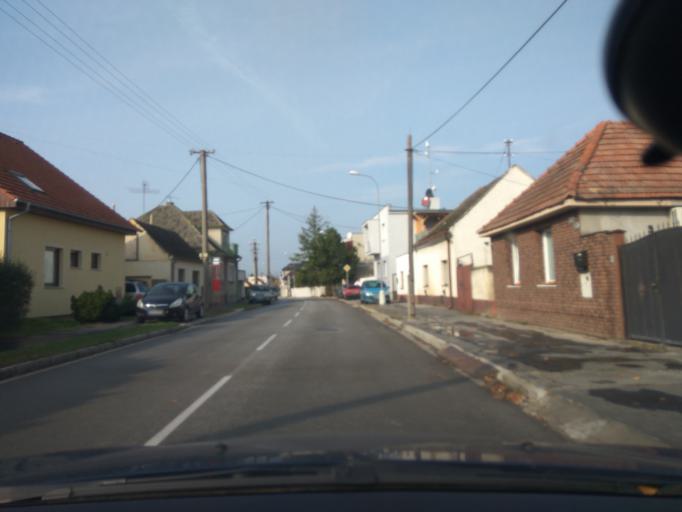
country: SK
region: Trnavsky
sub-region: Okres Trnava
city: Piestany
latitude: 48.6046
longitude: 17.8275
